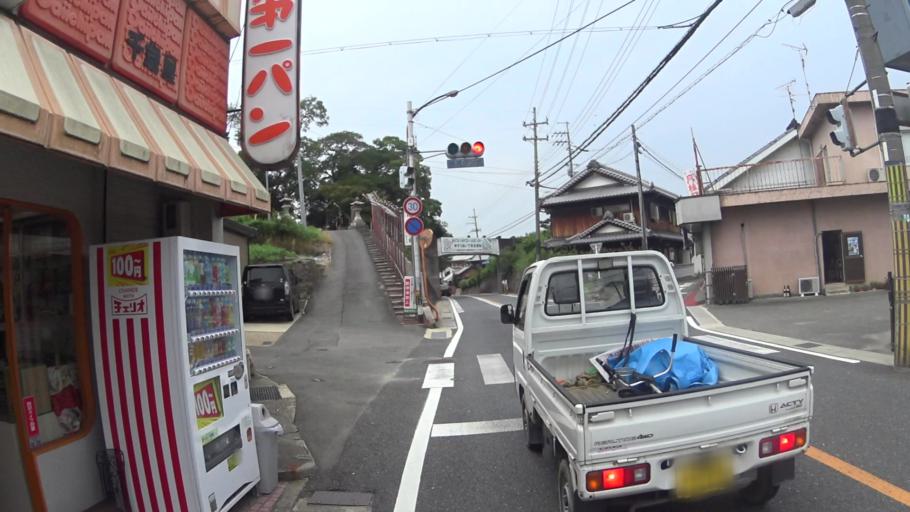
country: JP
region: Kyoto
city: Tanabe
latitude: 34.7964
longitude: 135.7847
